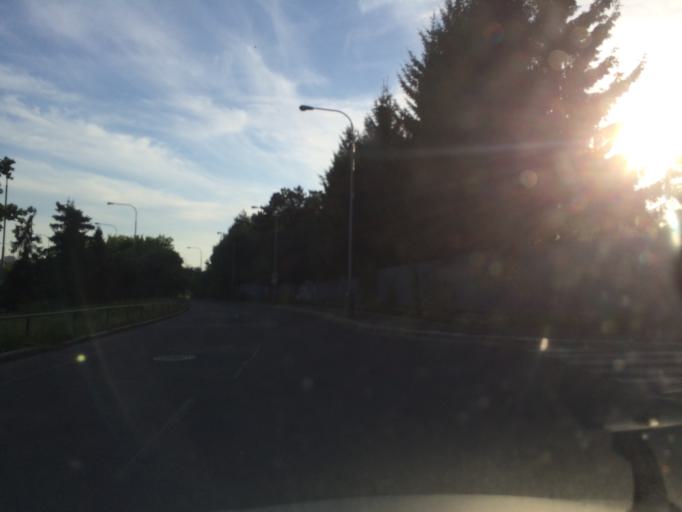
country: CZ
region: Praha
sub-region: Praha 4
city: Hodkovicky
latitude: 50.0392
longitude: 14.4572
